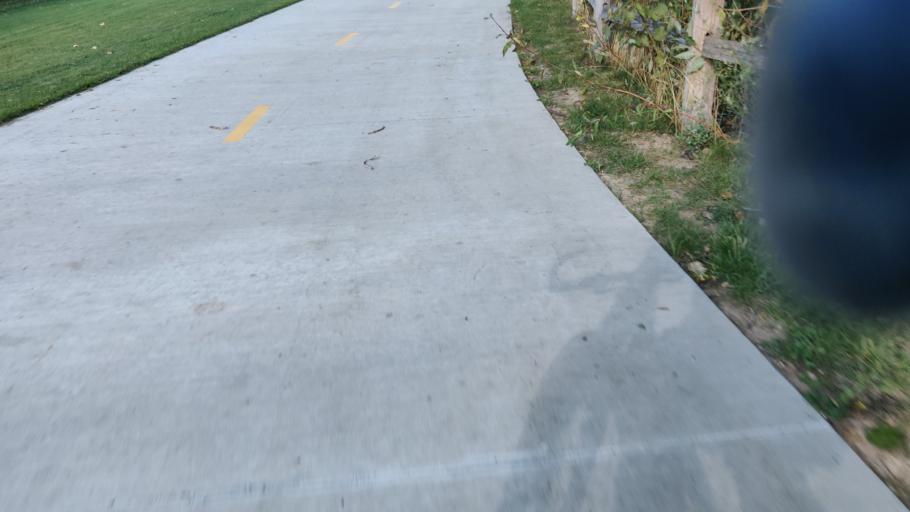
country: US
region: Idaho
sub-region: Ada County
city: Boise
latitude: 43.5714
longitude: -116.1409
